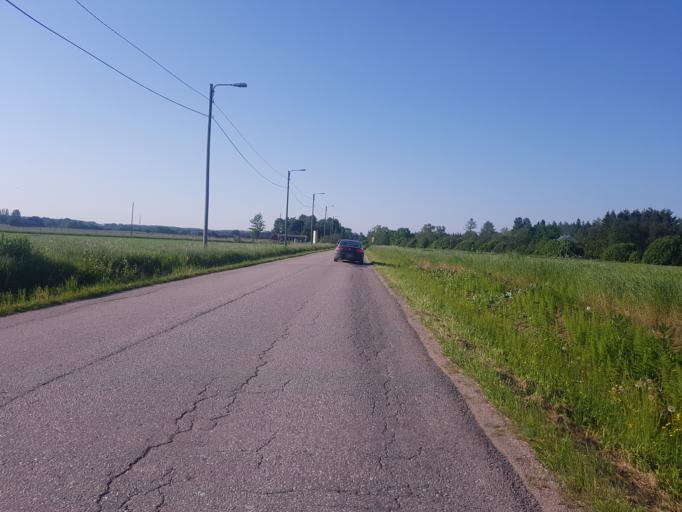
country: FI
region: Uusimaa
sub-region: Helsinki
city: Vantaa
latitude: 60.2692
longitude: 24.9566
